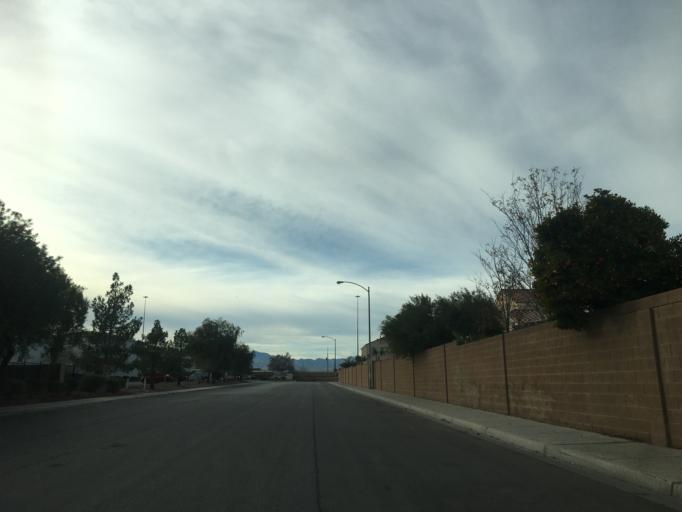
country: US
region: Nevada
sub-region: Clark County
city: Enterprise
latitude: 36.0154
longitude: -115.1772
